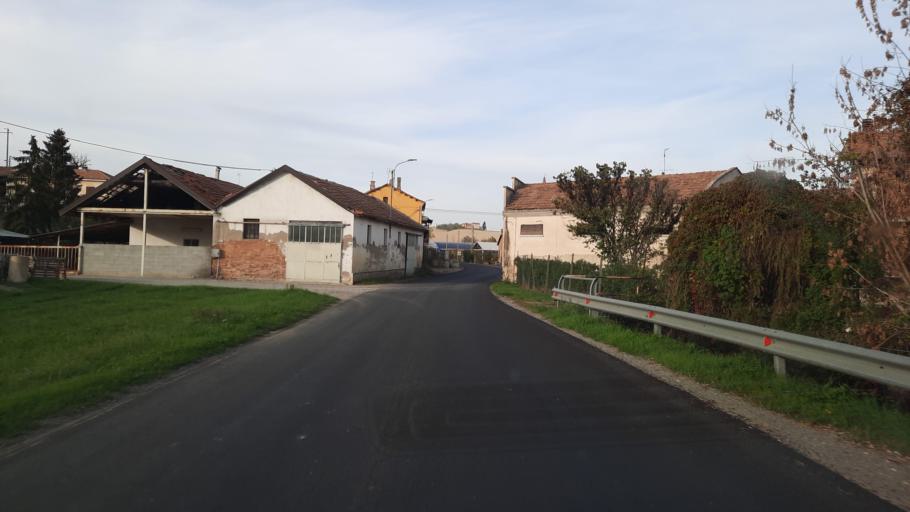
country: IT
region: Piedmont
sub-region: Provincia di Asti
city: Tonco
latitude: 45.0127
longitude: 8.2158
